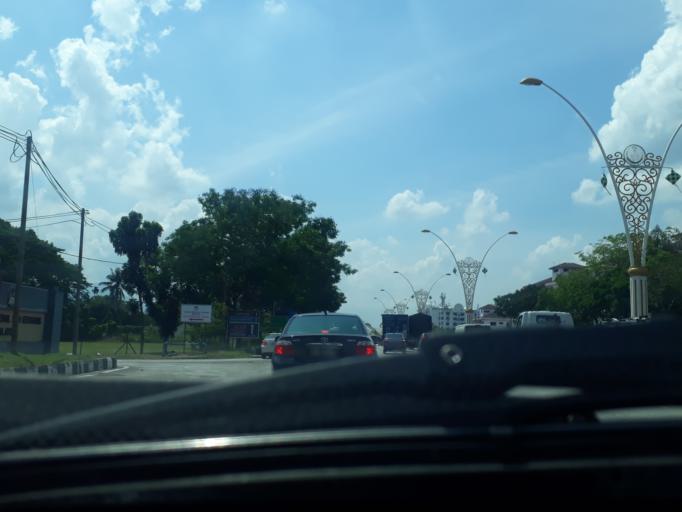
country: MY
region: Perak
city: Ipoh
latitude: 4.5982
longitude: 101.1200
